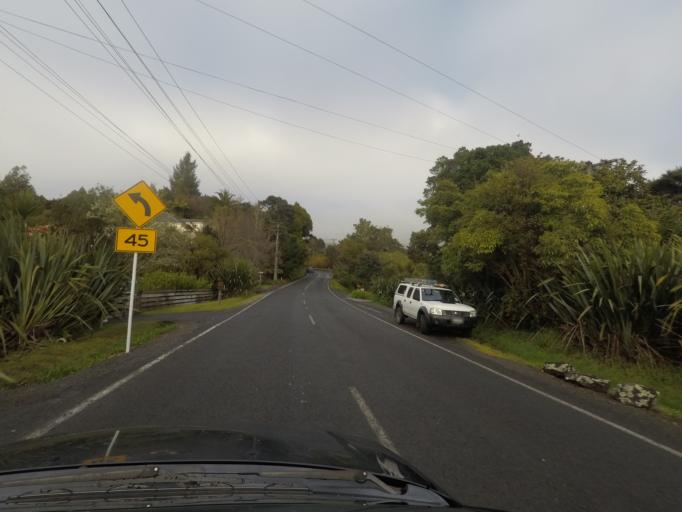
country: NZ
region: Auckland
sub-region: Auckland
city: Waitakere
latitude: -36.9204
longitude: 174.5853
